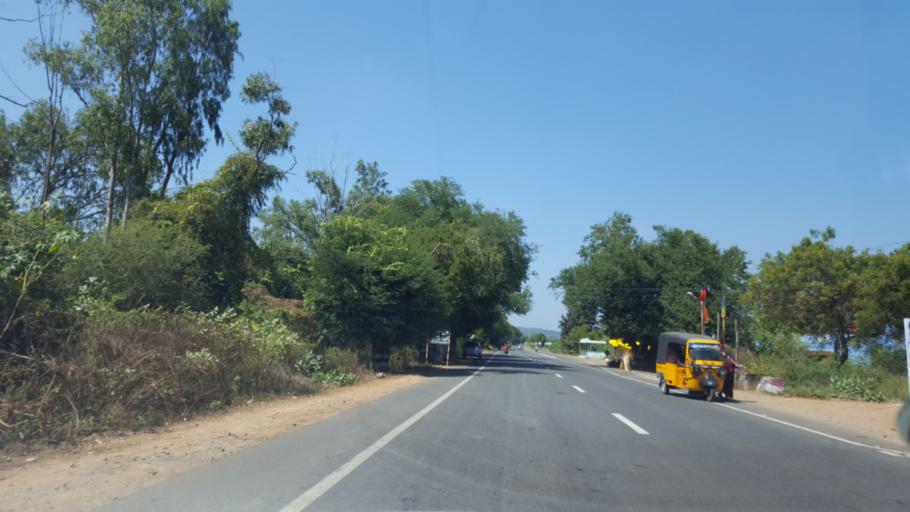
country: IN
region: Tamil Nadu
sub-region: Kancheepuram
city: Karumbakkam
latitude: 12.6261
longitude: 80.0518
